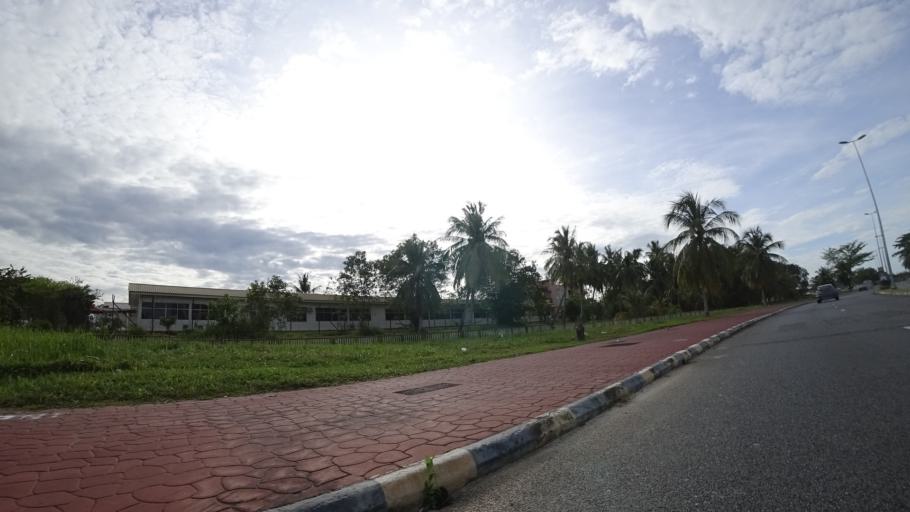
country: BN
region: Brunei and Muara
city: Bandar Seri Begawan
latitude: 4.9275
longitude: 114.9413
